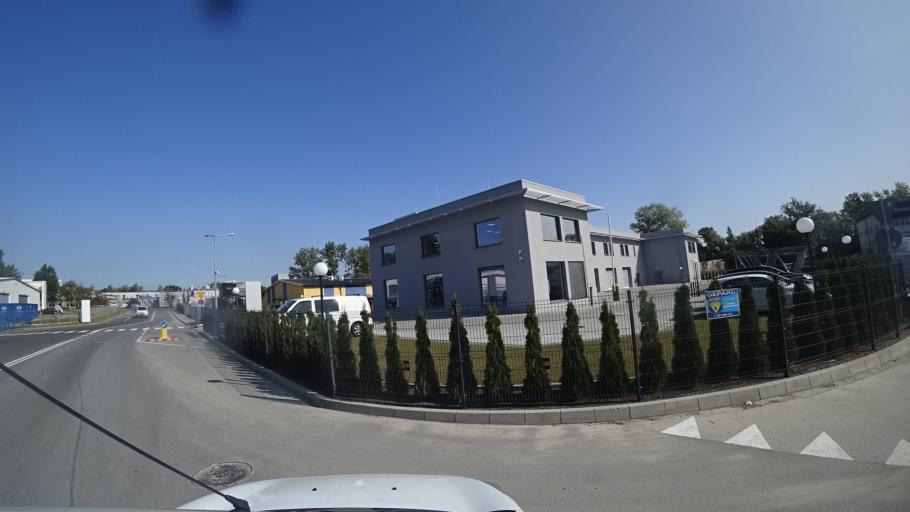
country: PL
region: Lesser Poland Voivodeship
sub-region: Krakow
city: Sidzina
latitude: 50.0052
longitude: 19.9005
